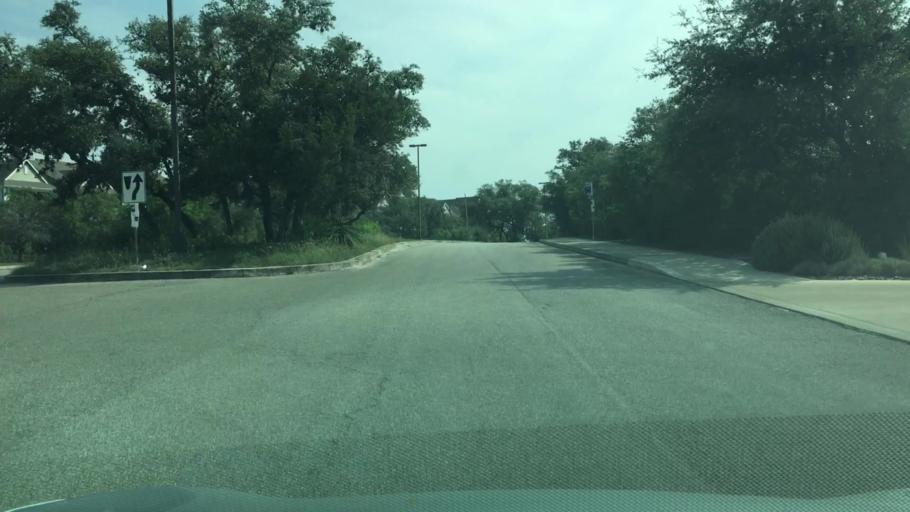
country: US
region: Texas
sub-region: Bexar County
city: Leon Valley
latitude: 29.4591
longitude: -98.6871
